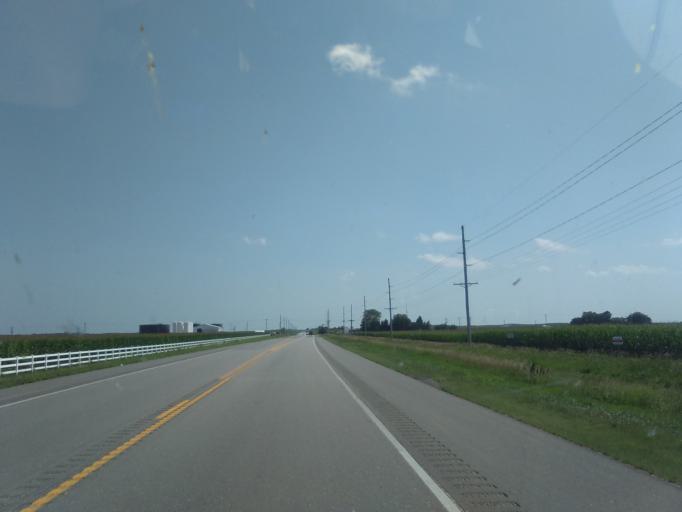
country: US
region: Nebraska
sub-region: Phelps County
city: Holdrege
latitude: 40.6617
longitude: -99.3803
